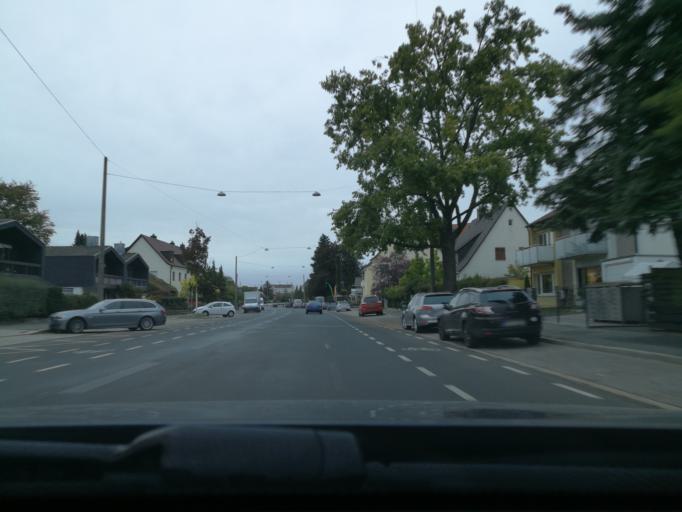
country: DE
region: Bavaria
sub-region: Regierungsbezirk Mittelfranken
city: Furth
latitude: 49.4763
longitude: 11.0074
